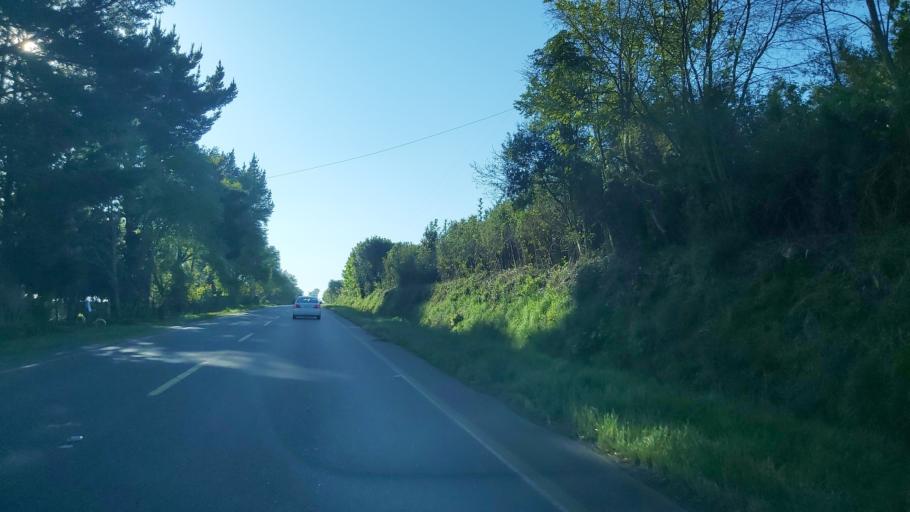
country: CL
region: Araucania
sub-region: Provincia de Malleco
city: Victoria
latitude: -38.2632
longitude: -72.2396
